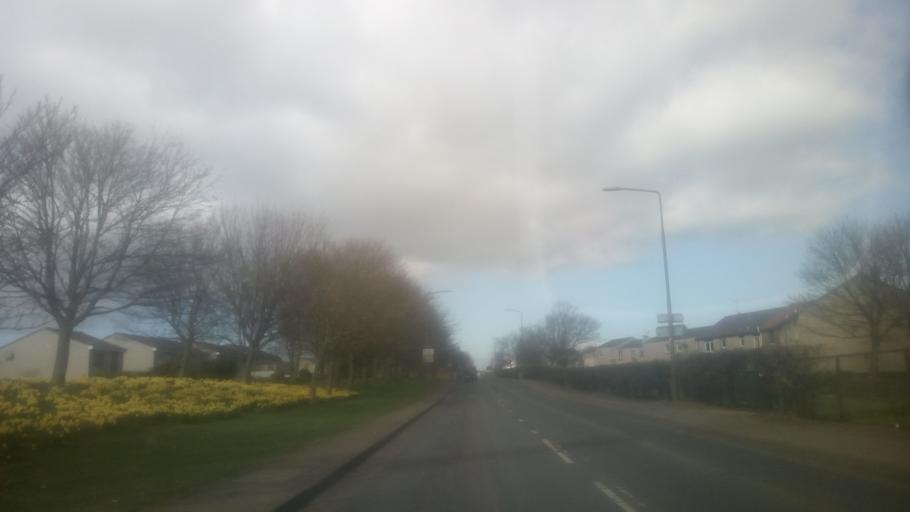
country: GB
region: Scotland
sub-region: East Lothian
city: Tranent
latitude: 55.9372
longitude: -2.9423
